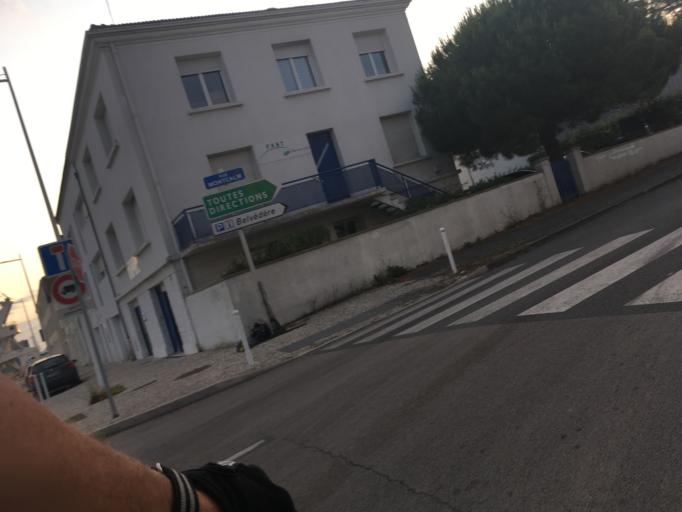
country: FR
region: Poitou-Charentes
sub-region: Departement de la Charente-Maritime
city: Rivedoux-Plage
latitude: 46.1606
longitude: -1.2199
